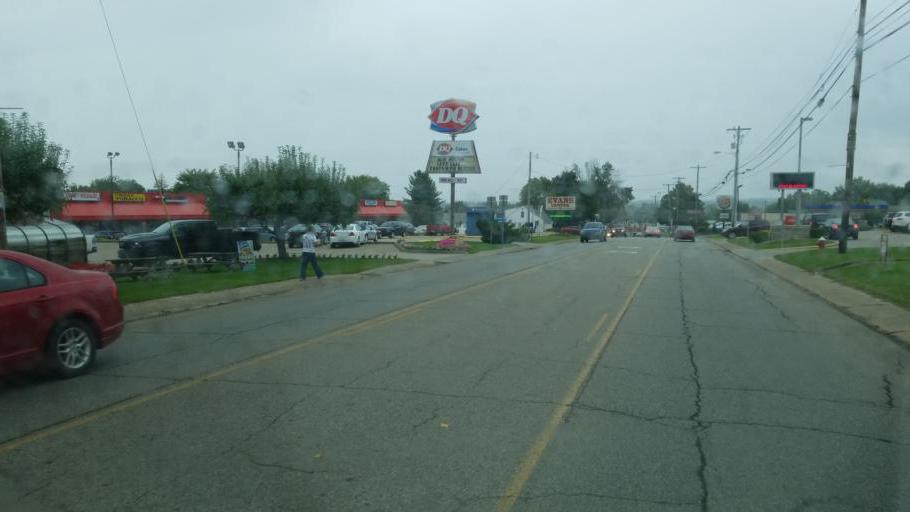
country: US
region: Ohio
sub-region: Jackson County
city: Jackson
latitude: 39.0415
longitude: -82.6286
